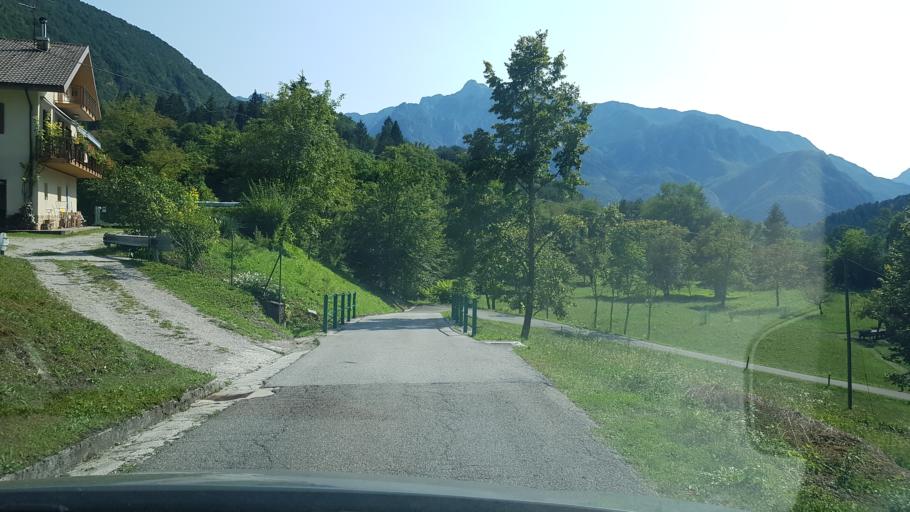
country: IT
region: Friuli Venezia Giulia
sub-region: Provincia di Udine
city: Moggio Udinese
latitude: 46.4267
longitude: 13.2057
